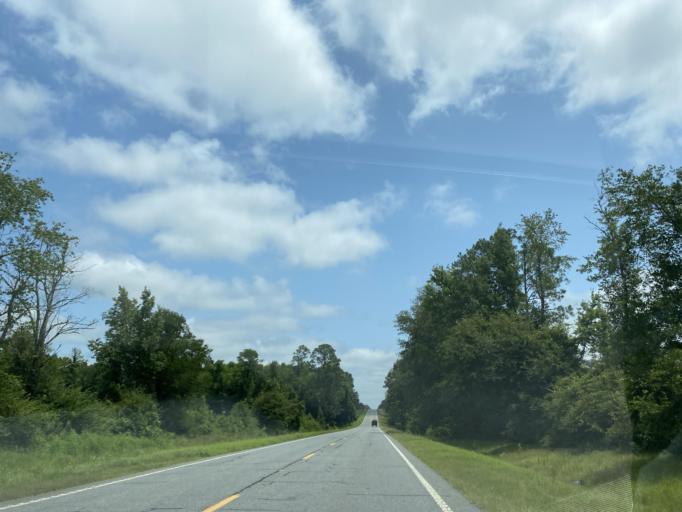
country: US
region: Georgia
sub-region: Wheeler County
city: Alamo
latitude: 32.1091
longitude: -82.8223
